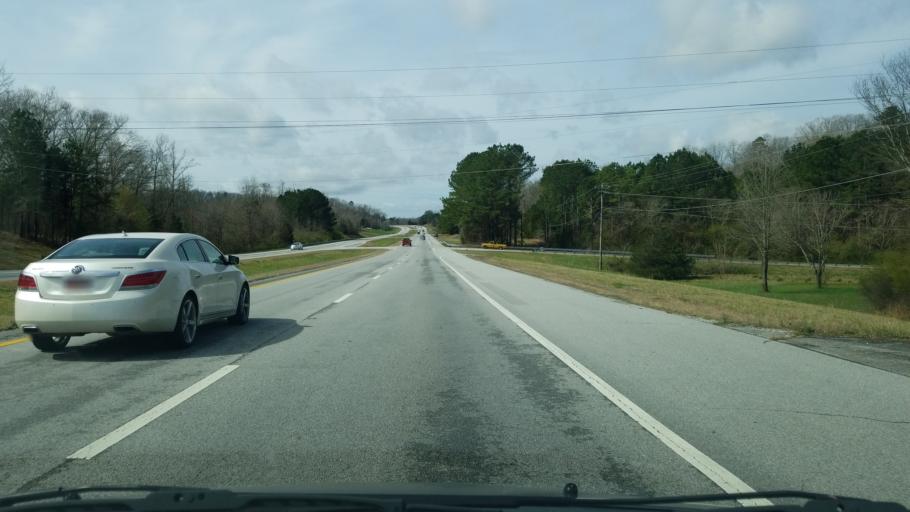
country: US
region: Tennessee
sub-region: Hamilton County
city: Lakesite
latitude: 35.1605
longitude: -85.0937
